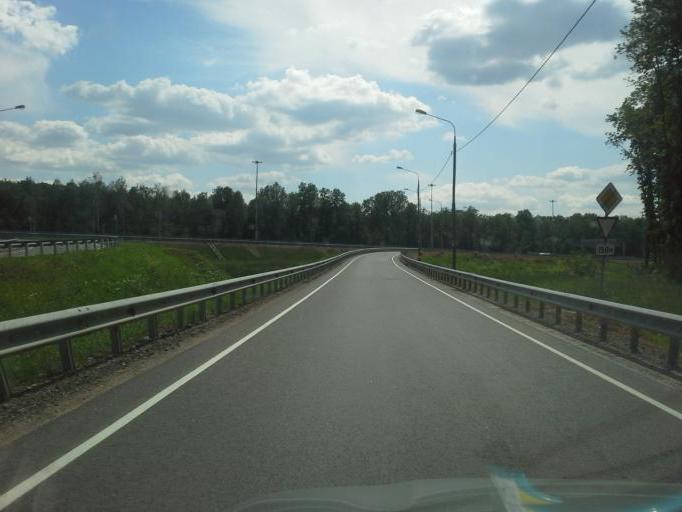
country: RU
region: Moskovskaya
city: Odintsovo
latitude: 55.6939
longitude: 37.2685
